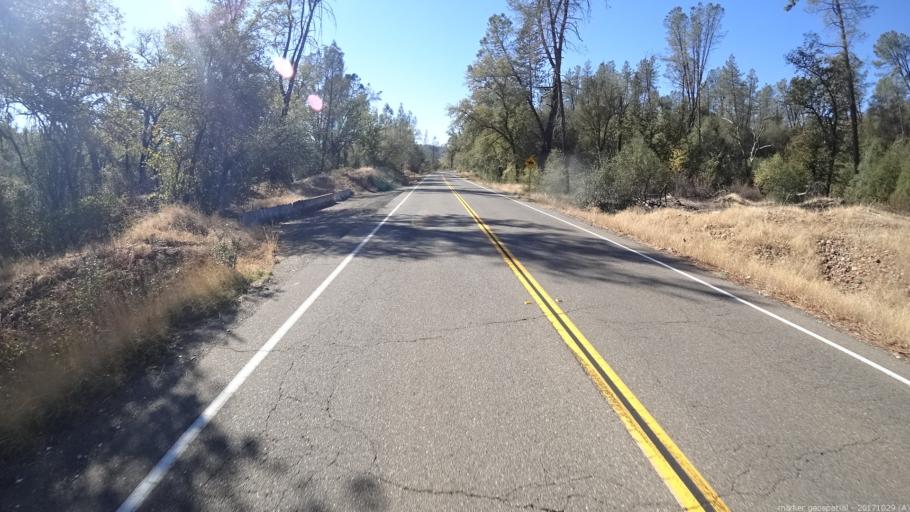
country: US
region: California
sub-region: Shasta County
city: Shasta
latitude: 40.4955
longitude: -122.4765
